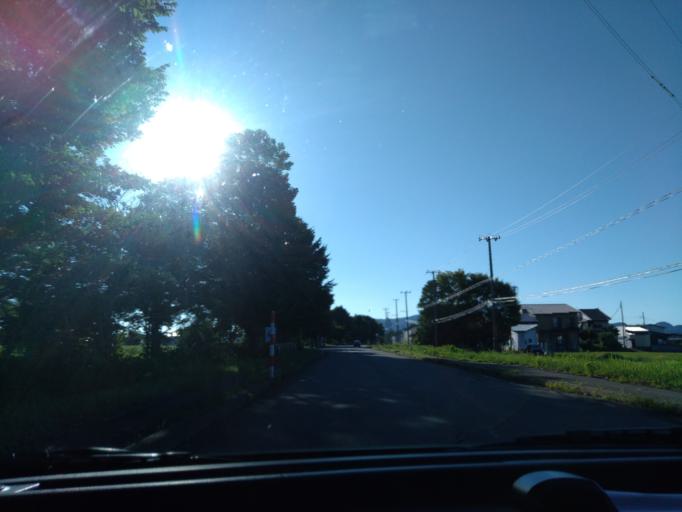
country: JP
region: Akita
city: Omagari
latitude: 39.4255
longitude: 140.4948
